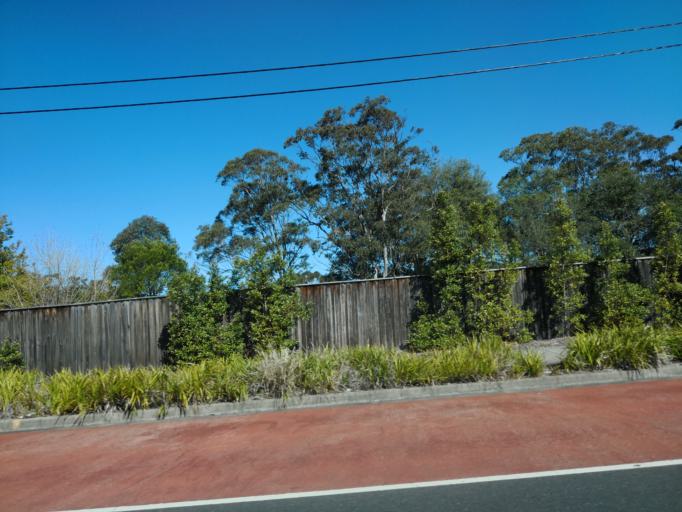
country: AU
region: New South Wales
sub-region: Gosford Shire
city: Erina
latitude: -33.4251
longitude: 151.4034
